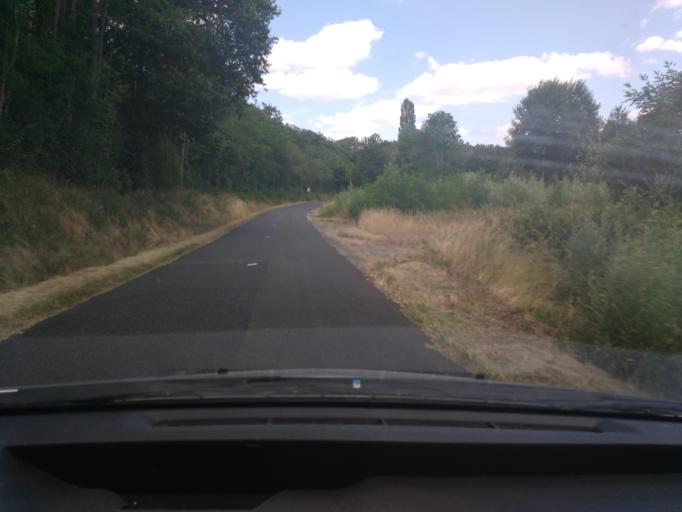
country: FR
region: Pays de la Loire
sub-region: Departement de Maine-et-Loire
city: Bauge-en-Anjou
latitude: 47.5484
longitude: -0.0737
